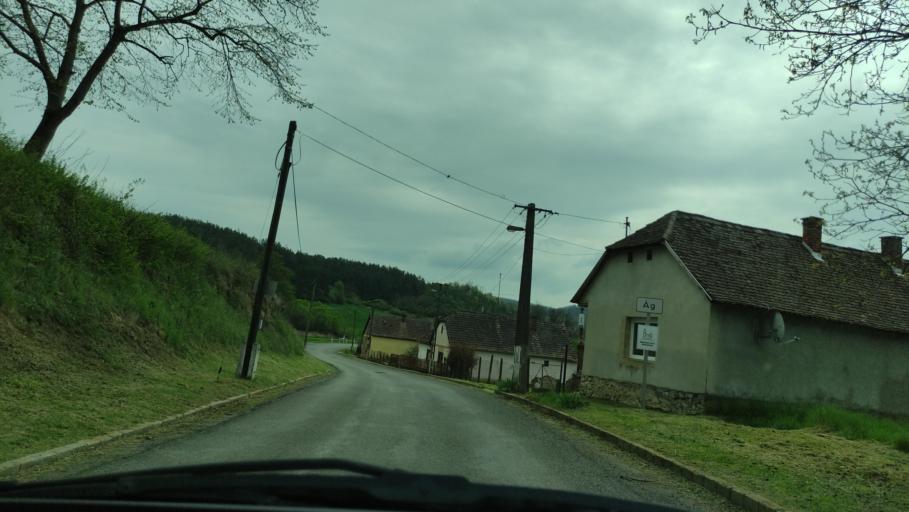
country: HU
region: Baranya
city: Magocs
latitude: 46.2997
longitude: 18.1974
